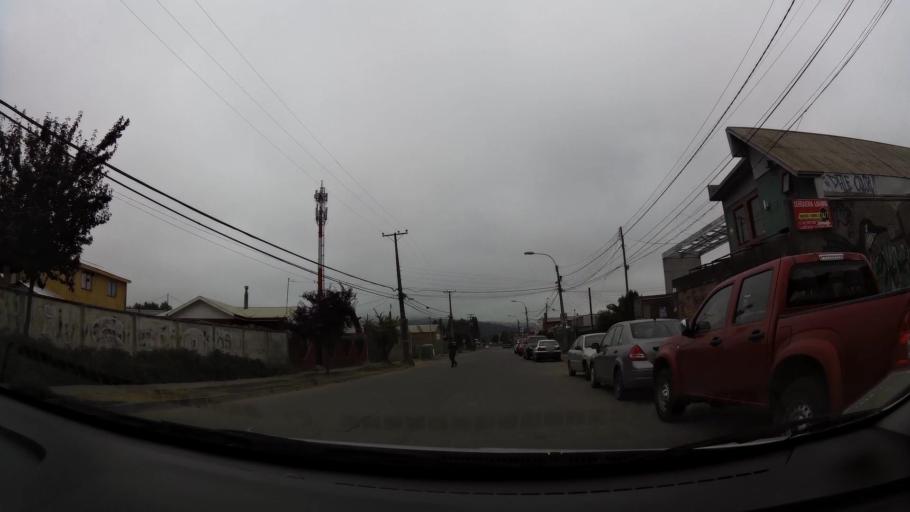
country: CL
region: Biobio
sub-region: Provincia de Concepcion
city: Concepcion
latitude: -36.8248
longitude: -72.9932
